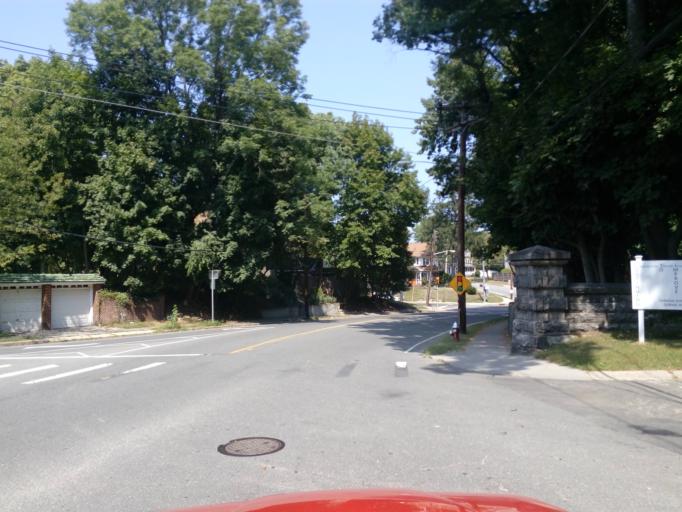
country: US
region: New York
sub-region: Nassau County
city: Glen Cove
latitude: 40.8680
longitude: -73.6355
